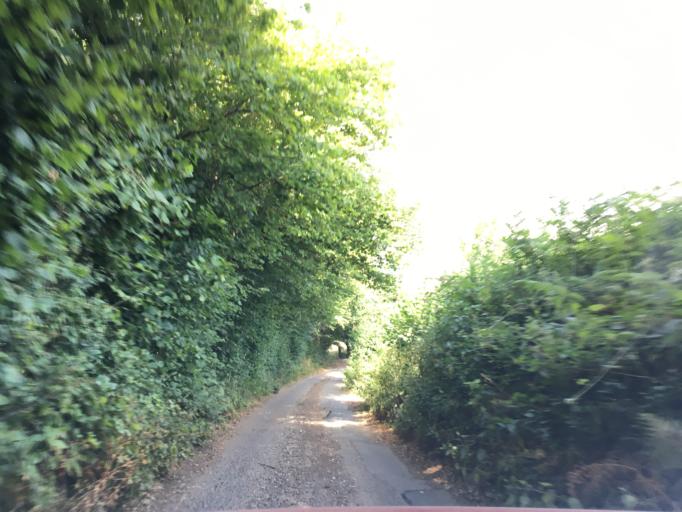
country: GB
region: Wales
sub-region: Caerphilly County Borough
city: Risca
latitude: 51.5960
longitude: -3.1000
